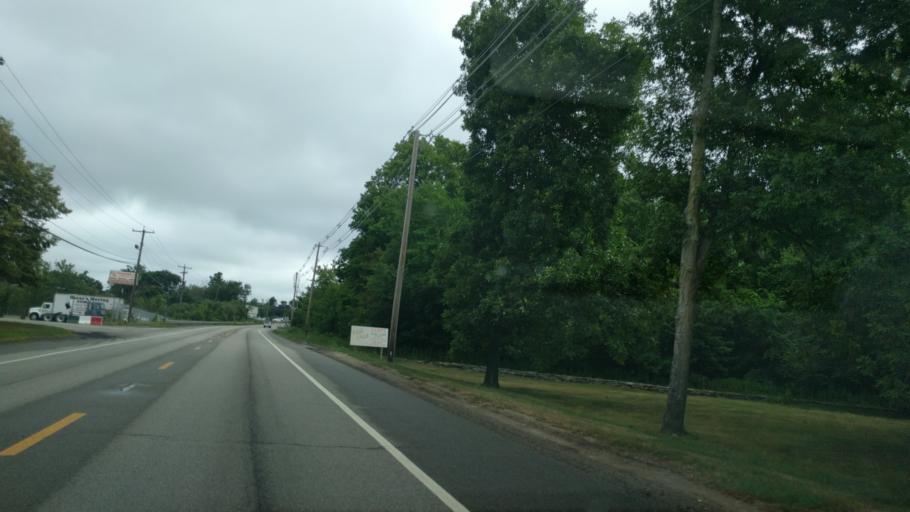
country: US
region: Massachusetts
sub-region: Worcester County
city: Shrewsbury
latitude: 42.2589
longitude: -71.7003
